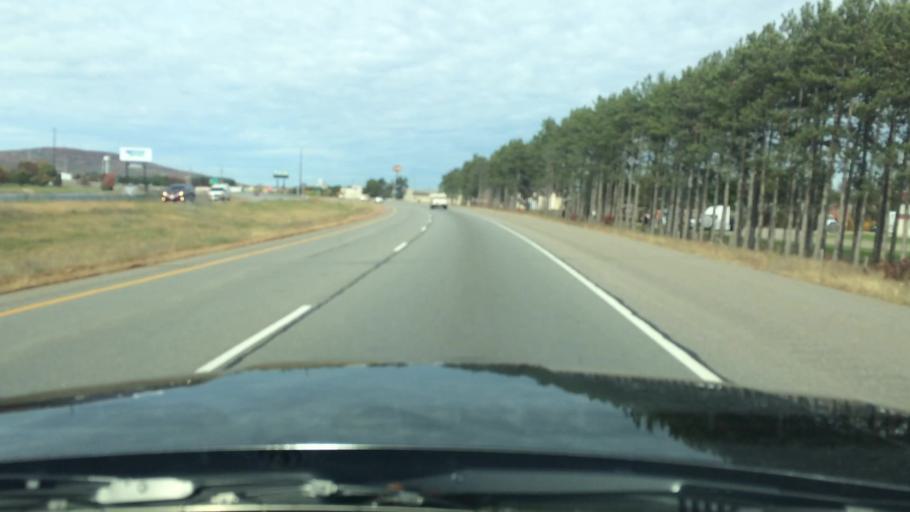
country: US
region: Wisconsin
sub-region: Marathon County
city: Evergreen
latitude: 44.8545
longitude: -89.6371
